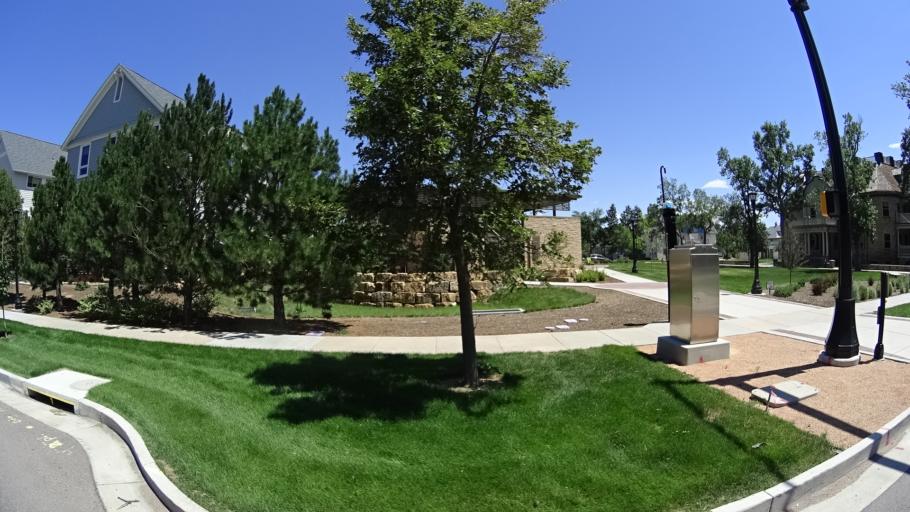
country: US
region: Colorado
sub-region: El Paso County
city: Colorado Springs
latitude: 38.8493
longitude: -104.8208
